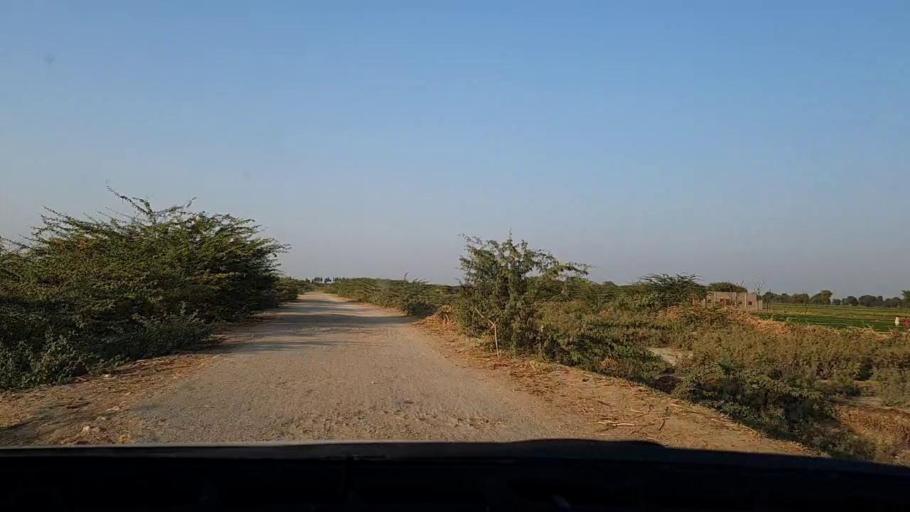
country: PK
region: Sindh
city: Tando Mittha Khan
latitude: 25.8650
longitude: 69.2726
